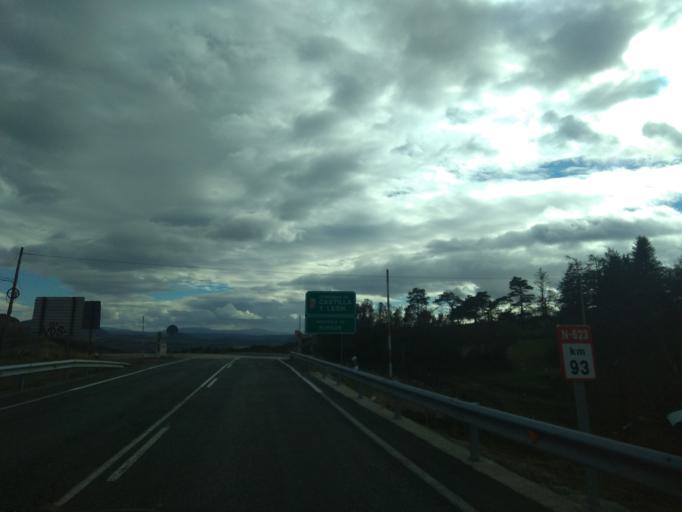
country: ES
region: Castille and Leon
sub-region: Provincia de Burgos
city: Arija
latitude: 43.0420
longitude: -3.8781
